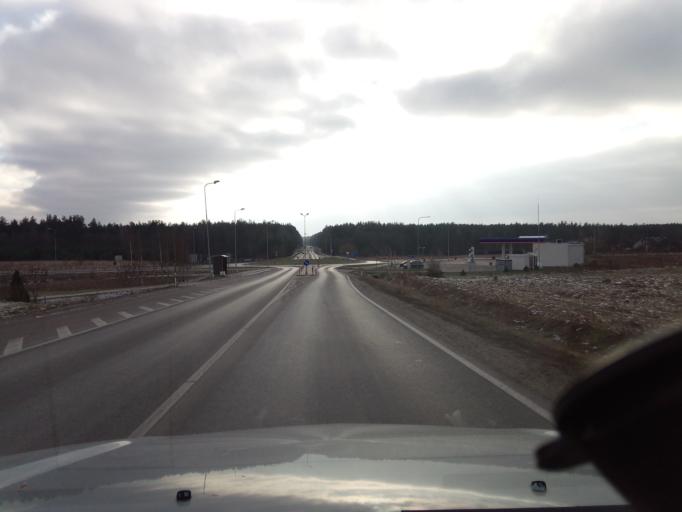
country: LT
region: Alytaus apskritis
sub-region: Alytaus rajonas
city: Daugai
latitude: 54.1701
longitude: 24.2084
